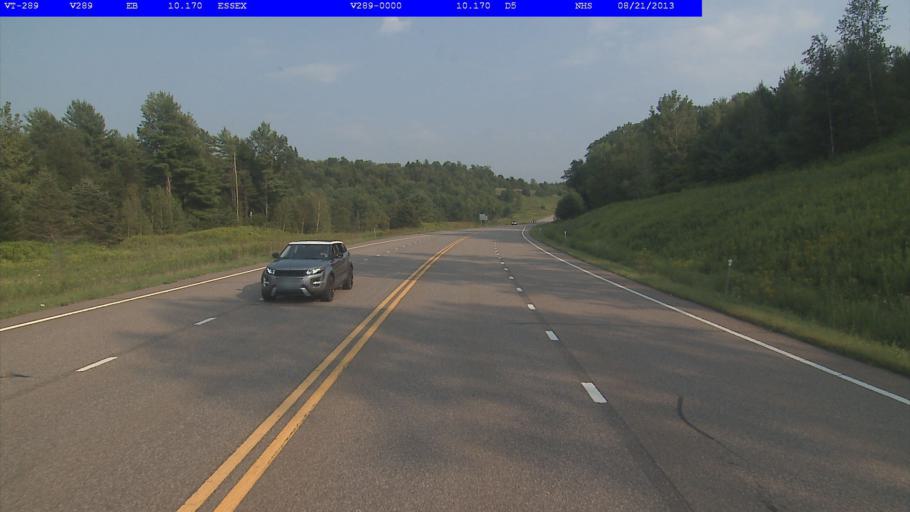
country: US
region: Vermont
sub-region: Chittenden County
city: Essex Junction
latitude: 44.5033
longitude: -73.0752
